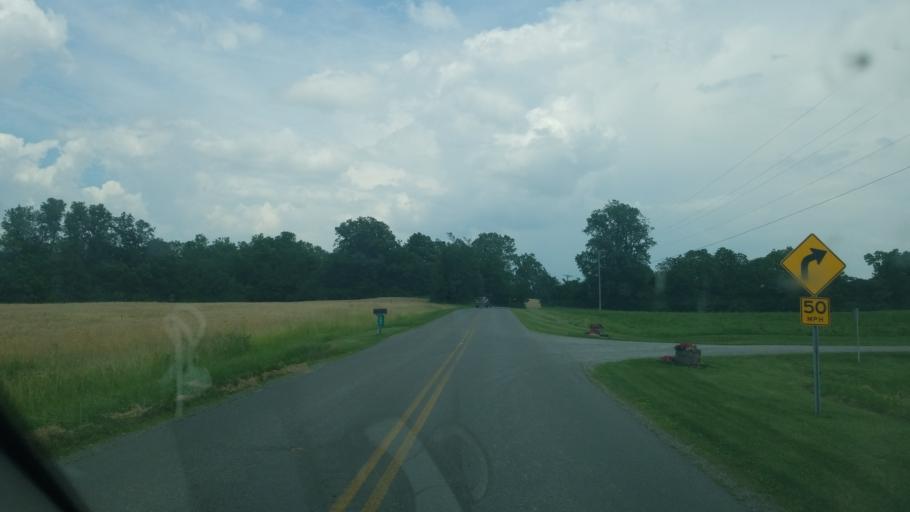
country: US
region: Ohio
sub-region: Logan County
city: Northwood
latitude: 40.4666
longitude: -83.7014
